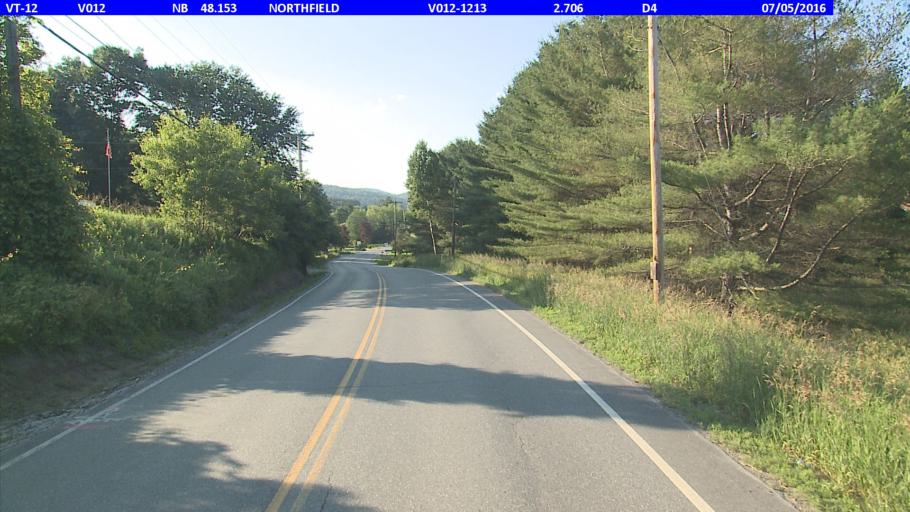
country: US
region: Vermont
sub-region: Washington County
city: Northfield
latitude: 44.1281
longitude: -72.6572
